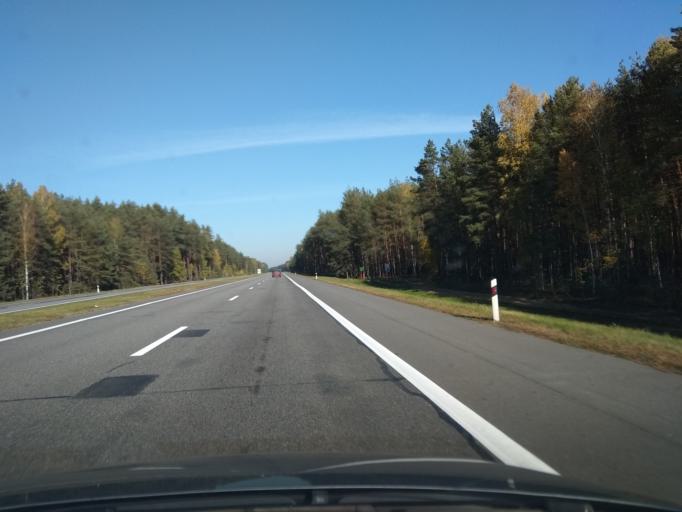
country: BY
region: Brest
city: Baranovichi
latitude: 52.9581
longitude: 25.7248
